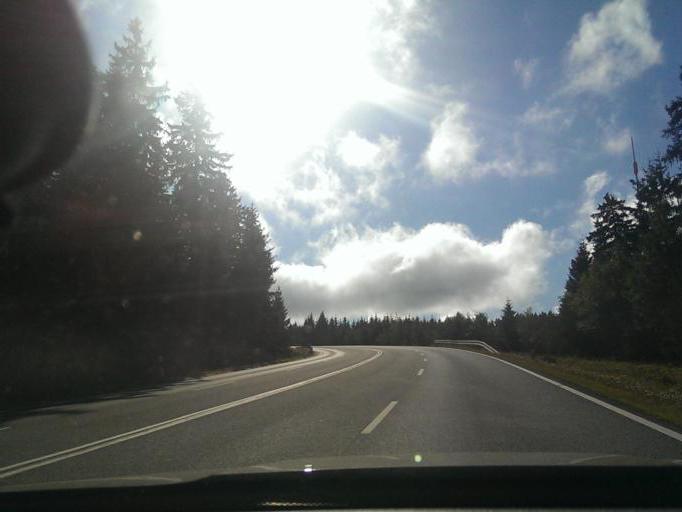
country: DE
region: Lower Saxony
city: Bad Harzburg
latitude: 51.8082
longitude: 10.5278
